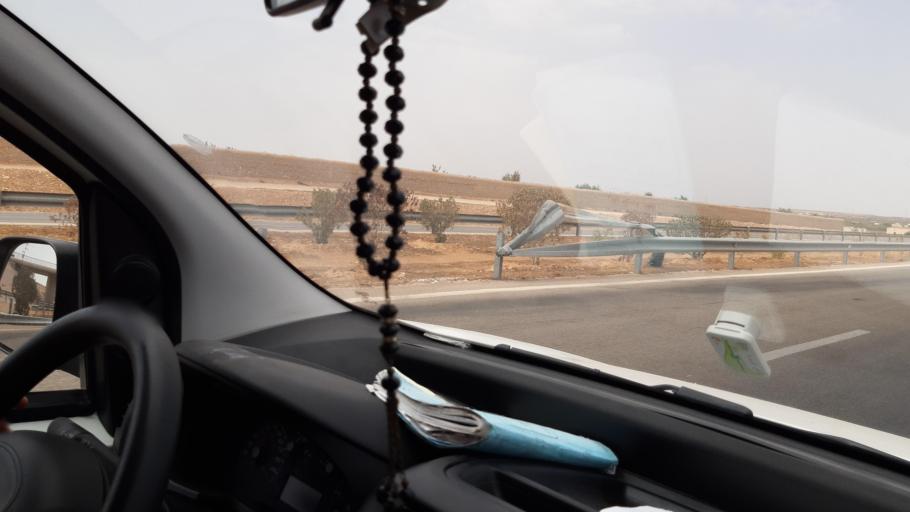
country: TN
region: Safaqis
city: Sfax
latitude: 34.8745
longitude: 10.6970
